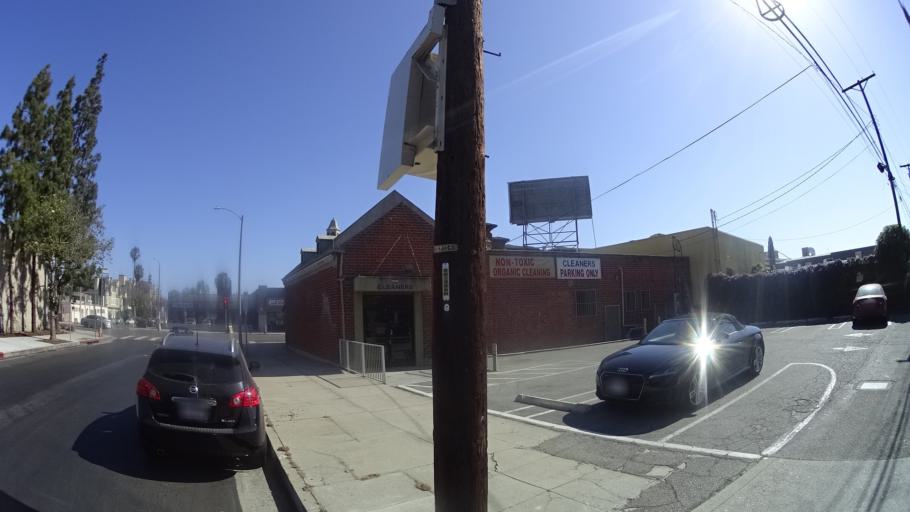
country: US
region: California
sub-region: Los Angeles County
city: West Hollywood
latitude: 34.0696
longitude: -118.3475
